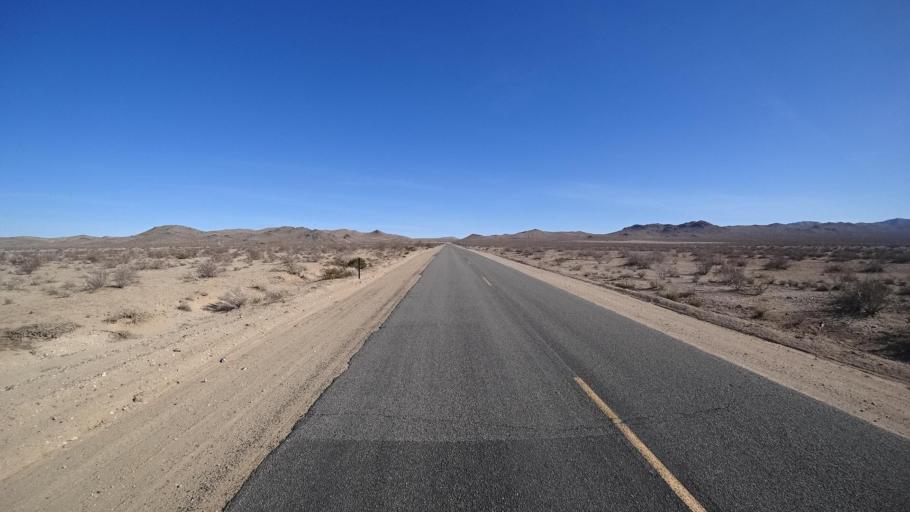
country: US
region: California
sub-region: Kern County
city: Ridgecrest
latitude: 35.5516
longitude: -117.7241
